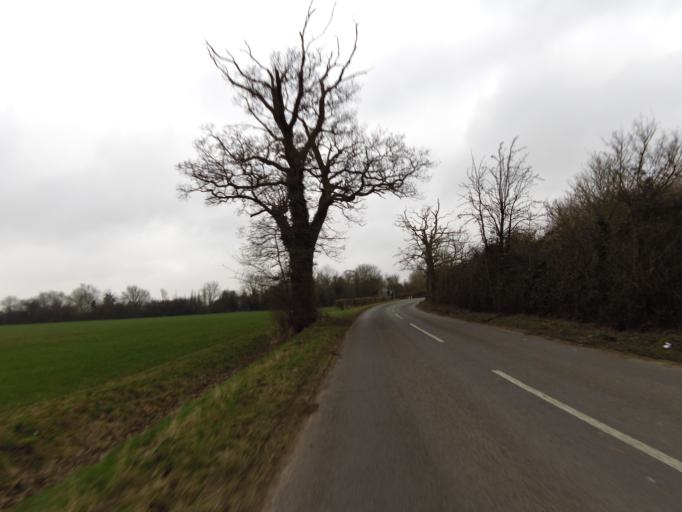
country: GB
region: England
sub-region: Suffolk
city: Framlingham
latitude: 52.1964
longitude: 1.3238
